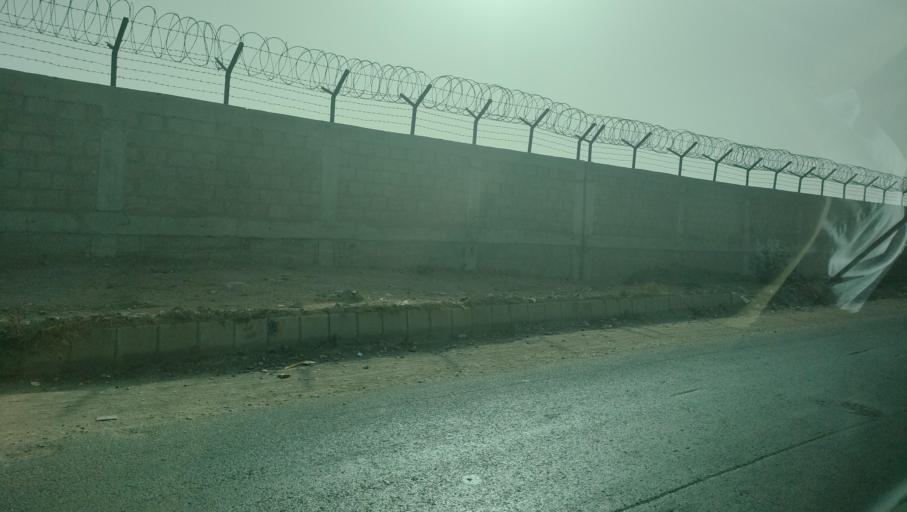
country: PK
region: Sindh
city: Malir Cantonment
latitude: 24.9215
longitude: 67.1853
